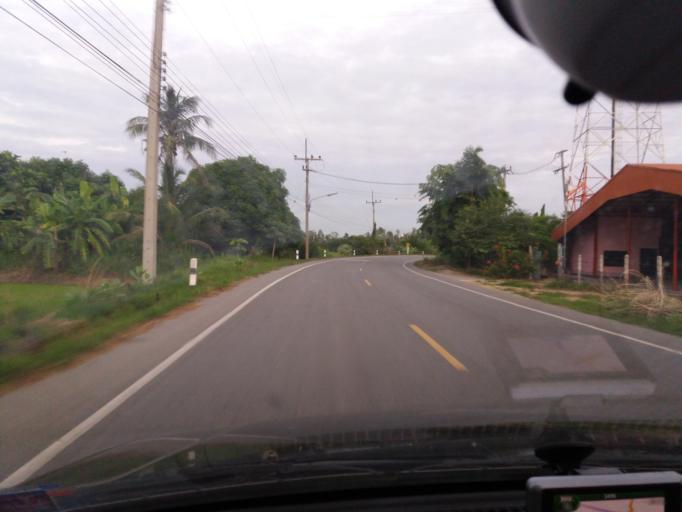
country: TH
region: Suphan Buri
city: Don Chedi
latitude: 14.7053
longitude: 100.0258
